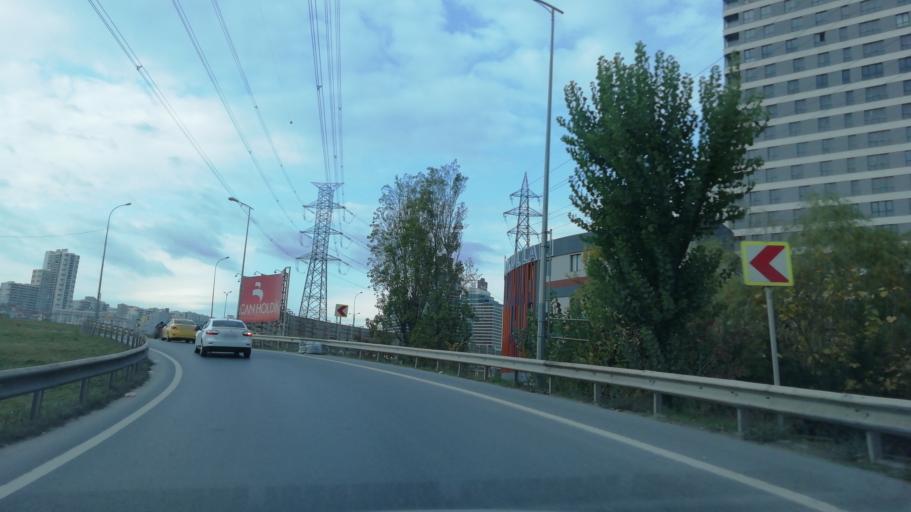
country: TR
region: Istanbul
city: Yakuplu
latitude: 41.0067
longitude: 28.6797
